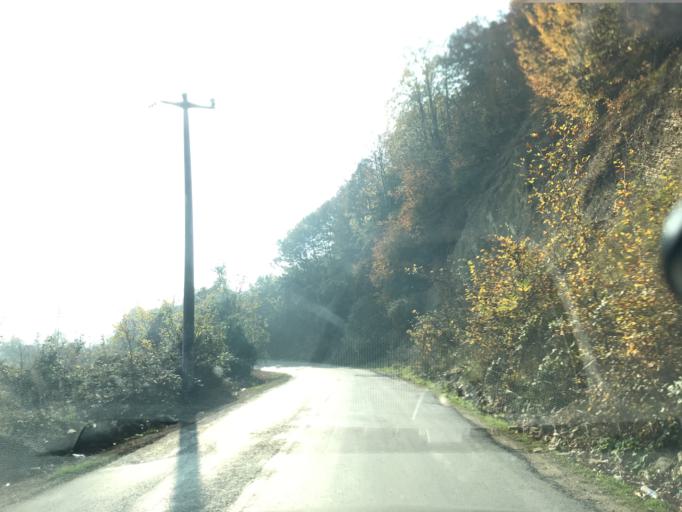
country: TR
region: Duzce
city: Cumayeri
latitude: 40.9116
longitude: 30.9445
